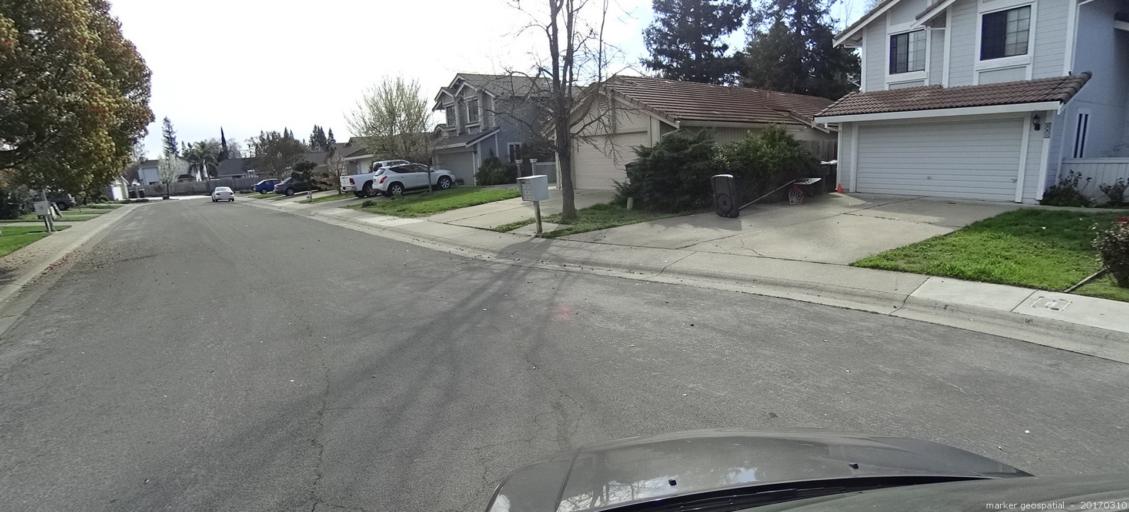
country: US
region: California
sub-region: Sacramento County
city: Parkway
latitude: 38.4845
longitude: -121.5394
